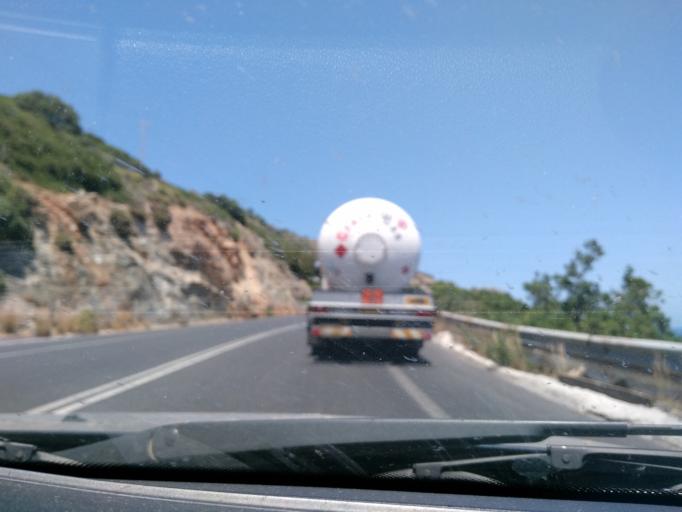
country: GR
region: Crete
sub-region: Nomos Irakleiou
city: Gazi
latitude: 35.3805
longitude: 25.0352
